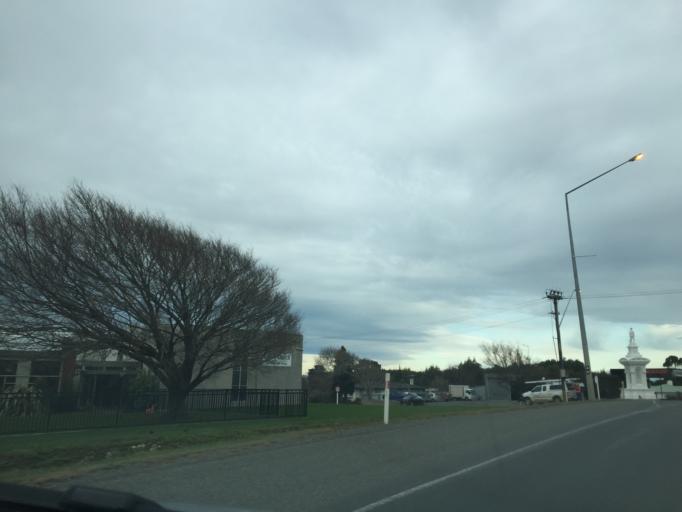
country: NZ
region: Southland
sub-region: Invercargill City
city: Invercargill
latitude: -46.3550
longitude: 168.5514
